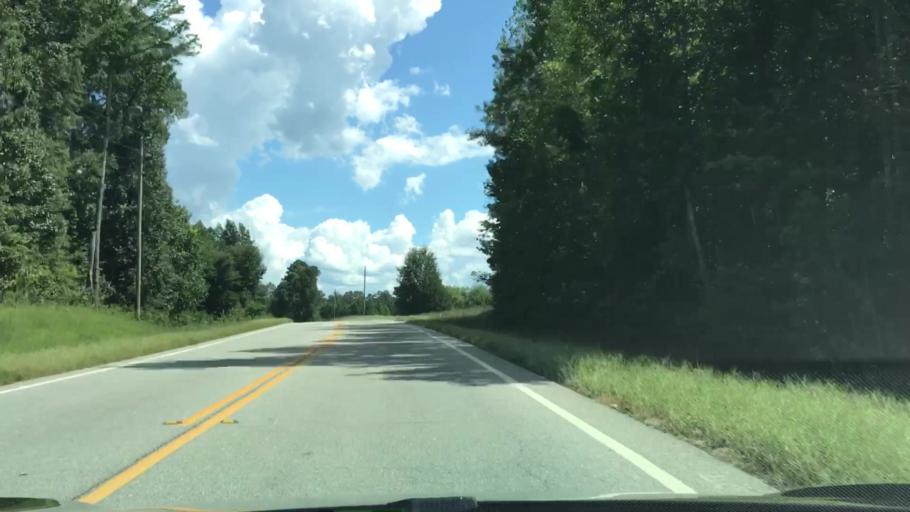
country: US
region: Georgia
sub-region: Greene County
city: Greensboro
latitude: 33.6682
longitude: -83.2582
